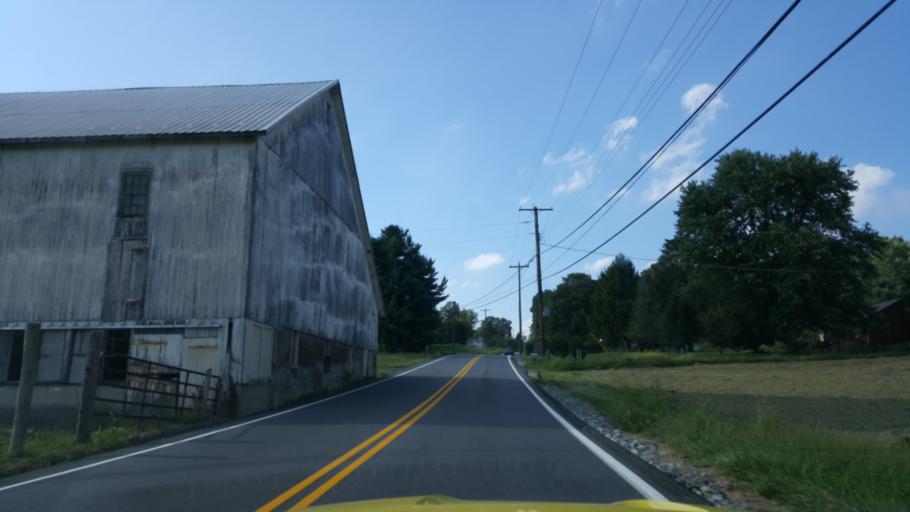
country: US
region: Pennsylvania
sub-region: Lebanon County
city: Campbelltown
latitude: 40.2541
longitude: -76.5490
